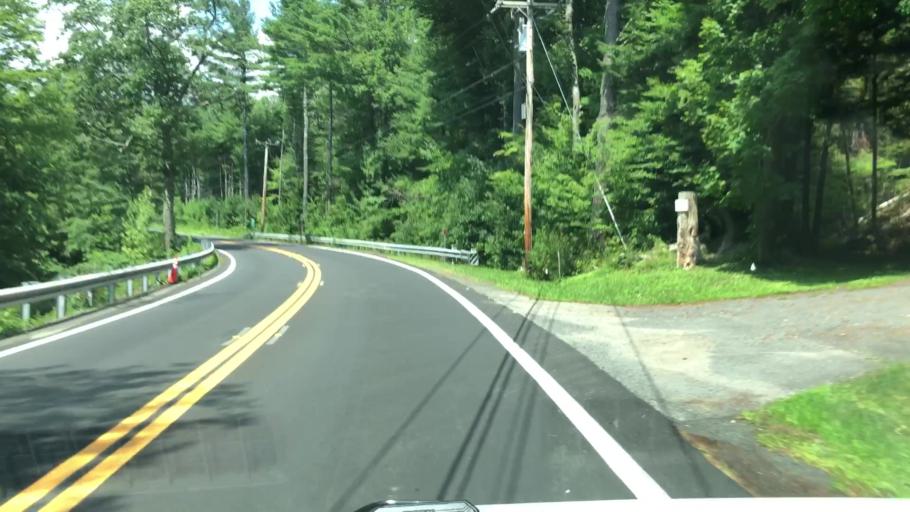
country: US
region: Massachusetts
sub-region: Franklin County
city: Ashfield
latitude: 42.5167
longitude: -72.7463
